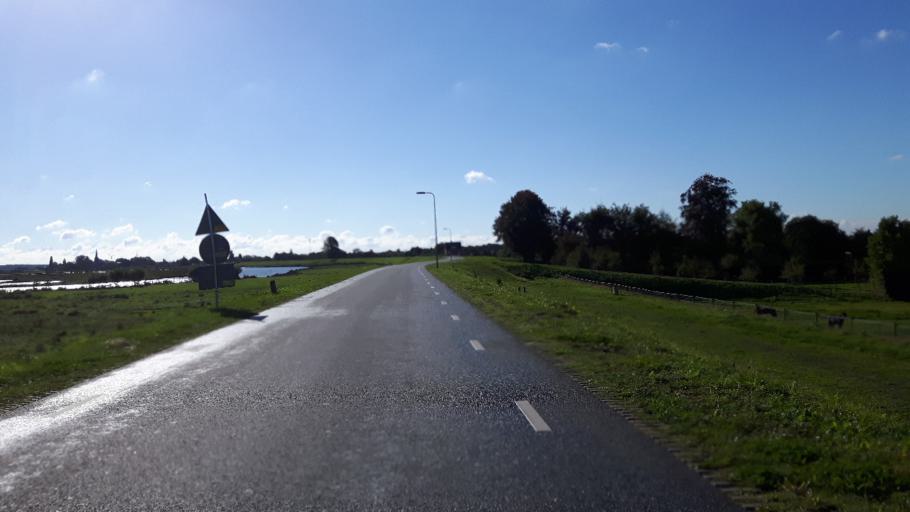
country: NL
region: Utrecht
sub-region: Gemeente Vianen
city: Vianen
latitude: 51.9758
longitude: 5.1444
